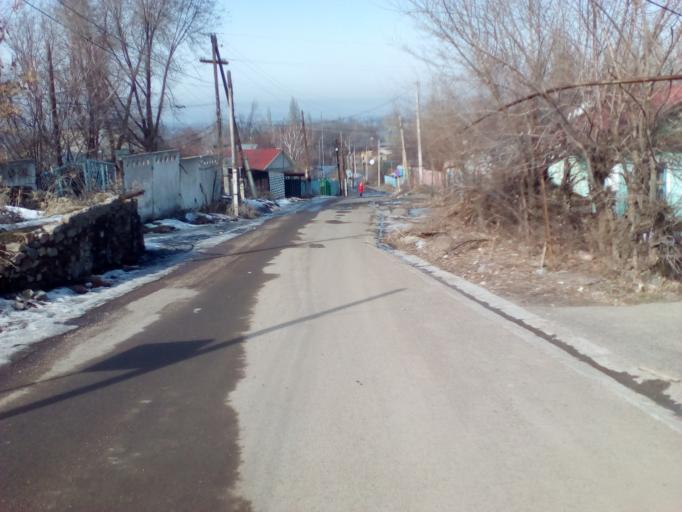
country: KZ
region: Almaty Oblysy
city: Burunday
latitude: 43.1527
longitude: 76.4179
